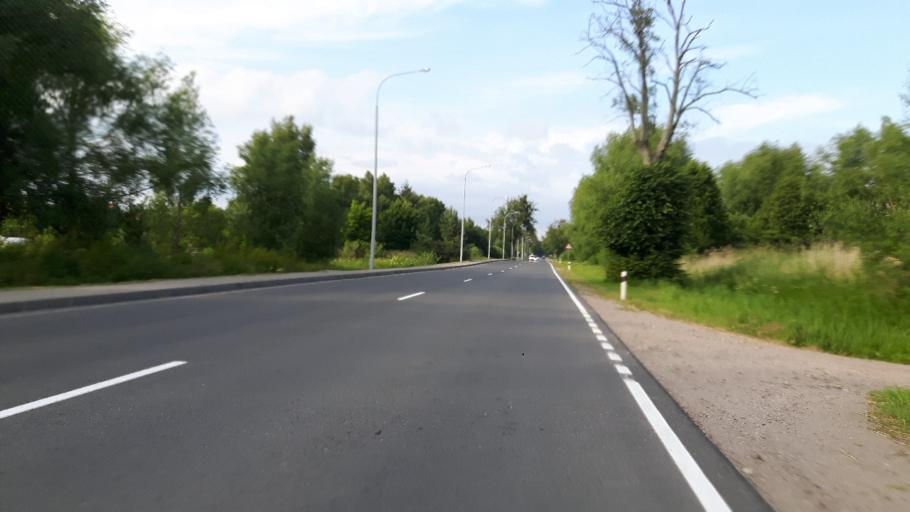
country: RU
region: Kaliningrad
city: Ladushkin
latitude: 54.5528
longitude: 20.1534
